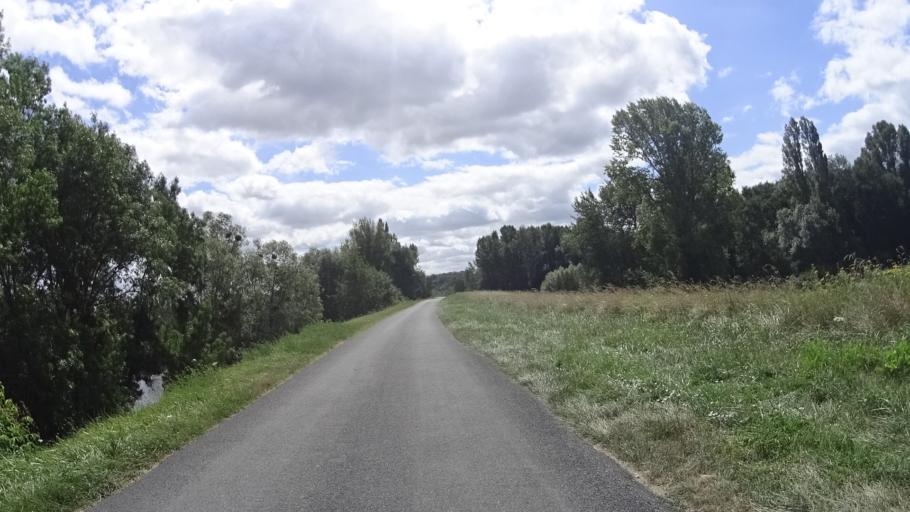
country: FR
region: Centre
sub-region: Departement d'Indre-et-Loire
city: Cinq-Mars-la-Pile
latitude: 47.3408
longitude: 0.4820
